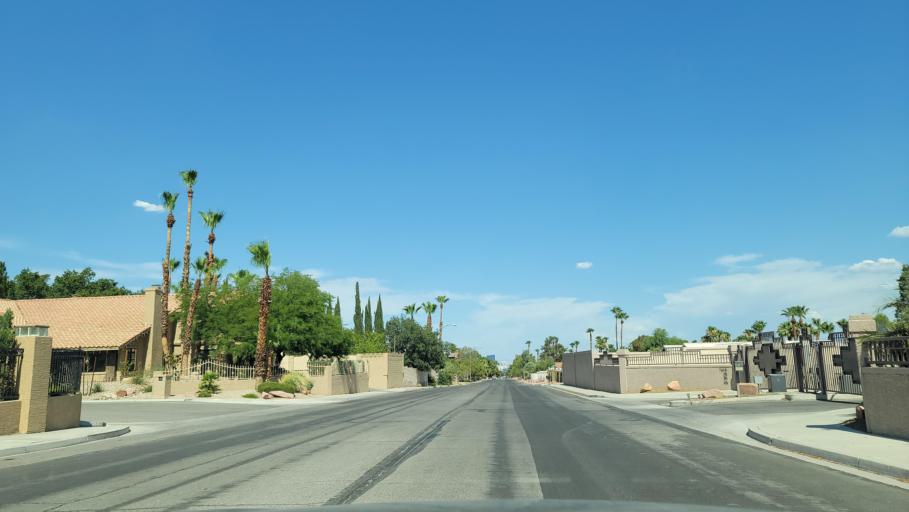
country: US
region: Nevada
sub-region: Clark County
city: Spring Valley
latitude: 36.1347
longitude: -115.2585
